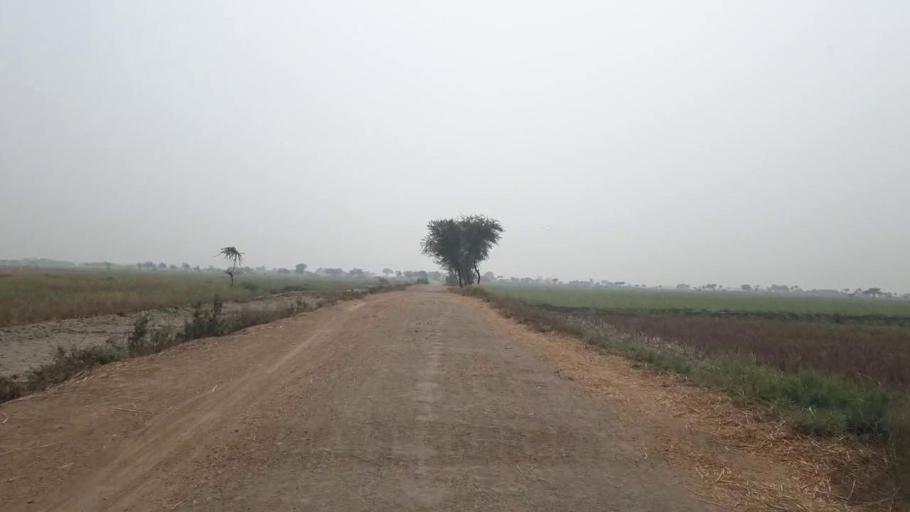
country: PK
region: Sindh
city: Kario
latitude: 24.6510
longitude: 68.6217
